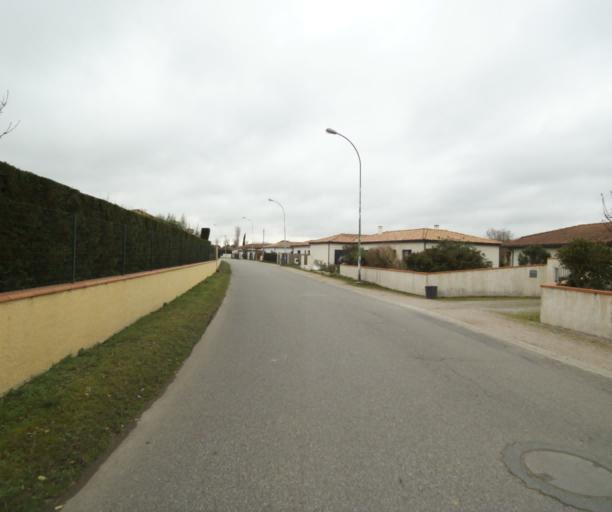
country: FR
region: Midi-Pyrenees
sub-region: Departement de l'Ariege
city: Mazeres
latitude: 43.2496
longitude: 1.6719
